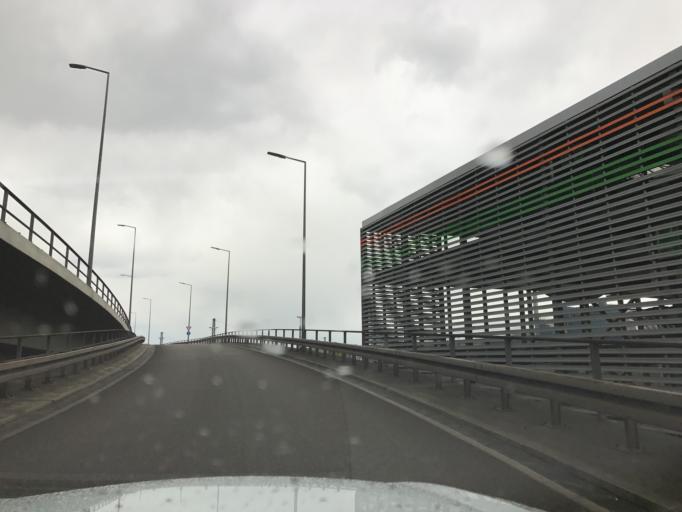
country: DE
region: Saarland
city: Volklingen
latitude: 49.2486
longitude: 6.8516
